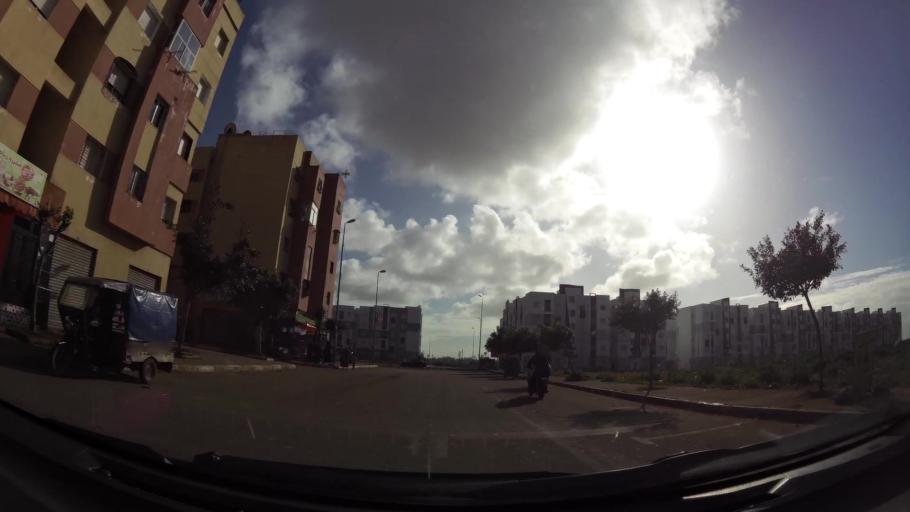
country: MA
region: Grand Casablanca
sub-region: Casablanca
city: Casablanca
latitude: 33.5512
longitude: -7.7056
